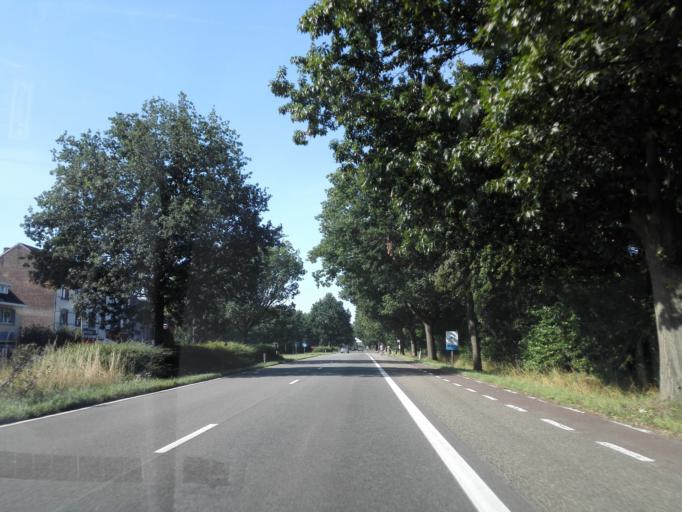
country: BE
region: Flanders
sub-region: Provincie Limburg
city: Genk
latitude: 51.0198
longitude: 5.5231
